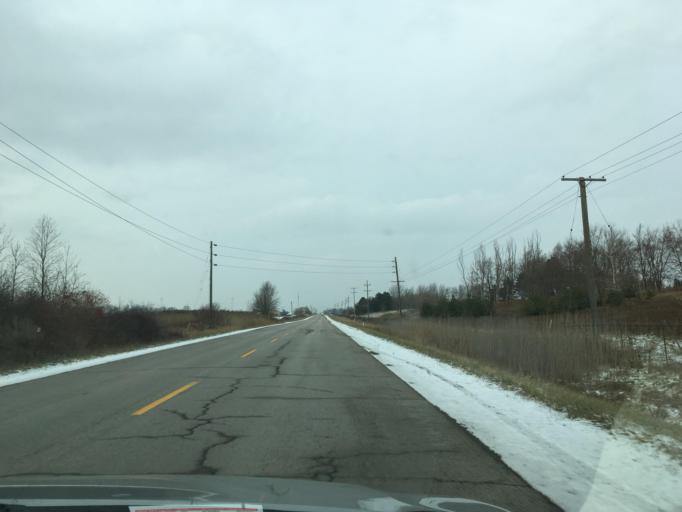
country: CA
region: Ontario
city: Norfolk County
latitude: 42.8057
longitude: -80.0606
